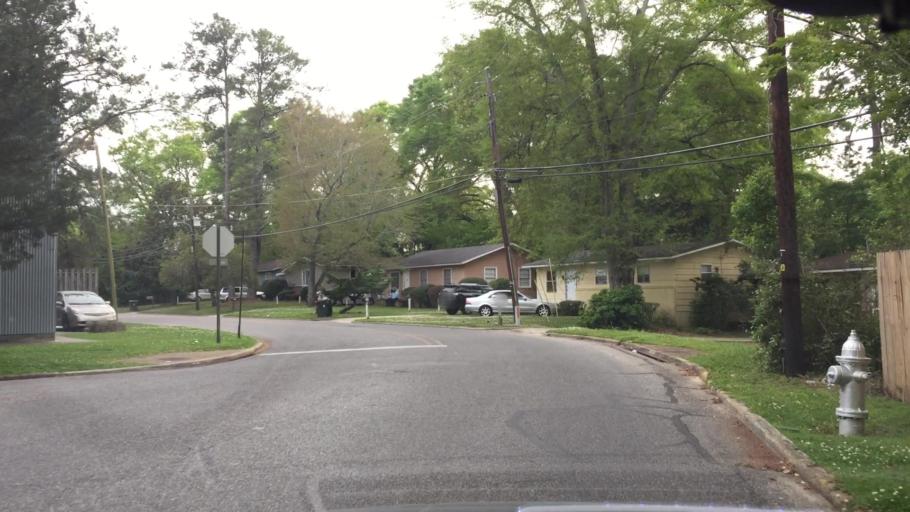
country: US
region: Alabama
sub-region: Lee County
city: Auburn
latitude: 32.6162
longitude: -85.4756
